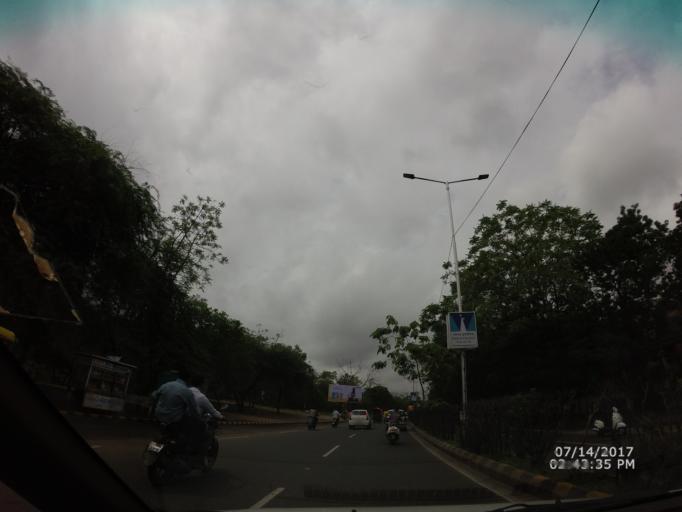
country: IN
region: Gujarat
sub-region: Ahmadabad
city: Ahmedabad
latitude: 23.0668
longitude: 72.6006
